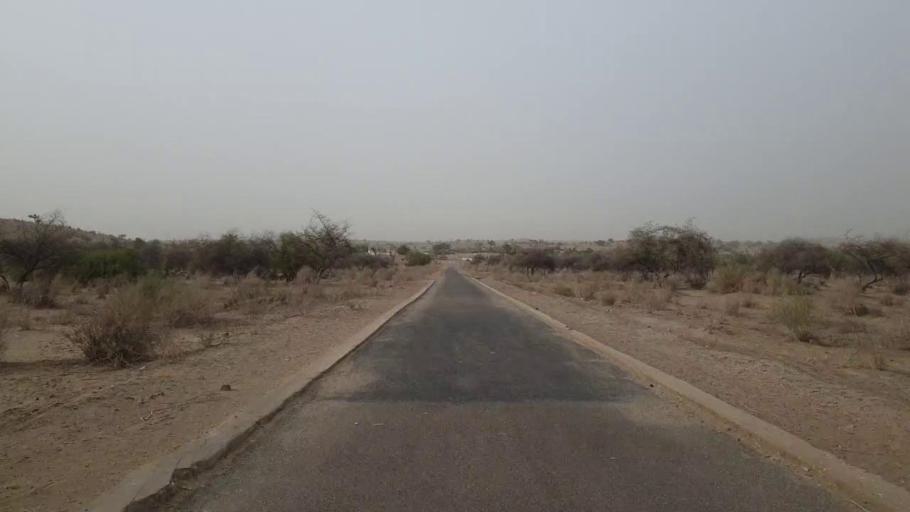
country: PK
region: Sindh
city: Islamkot
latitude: 24.5704
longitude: 70.3645
